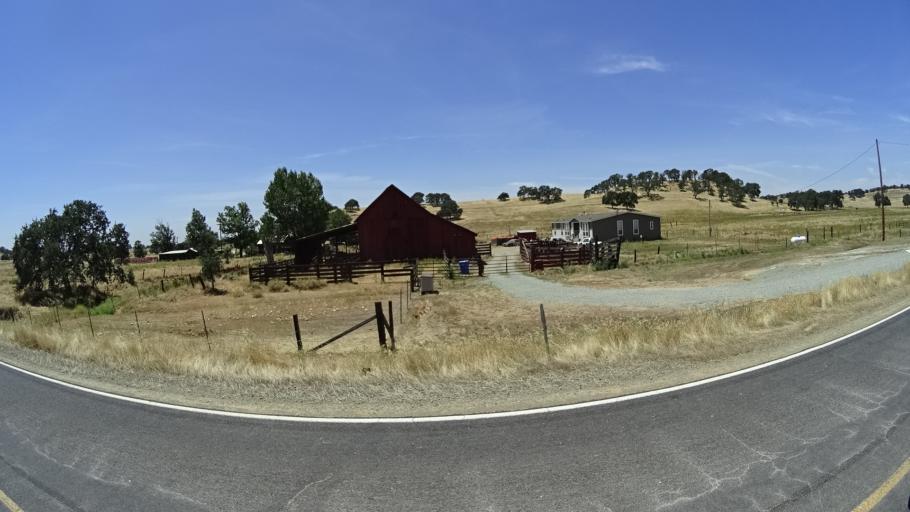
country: US
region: California
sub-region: Calaveras County
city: Rancho Calaveras
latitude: 38.1116
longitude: -120.8792
